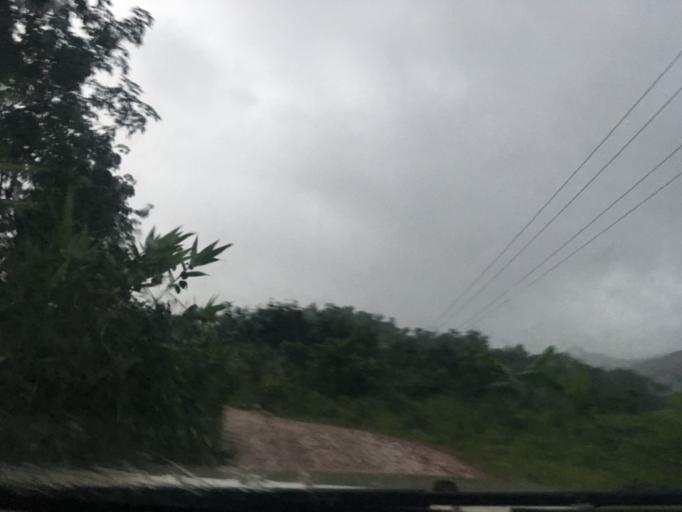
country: LA
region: Oudomxai
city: Muang La
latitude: 21.2500
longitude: 101.9327
